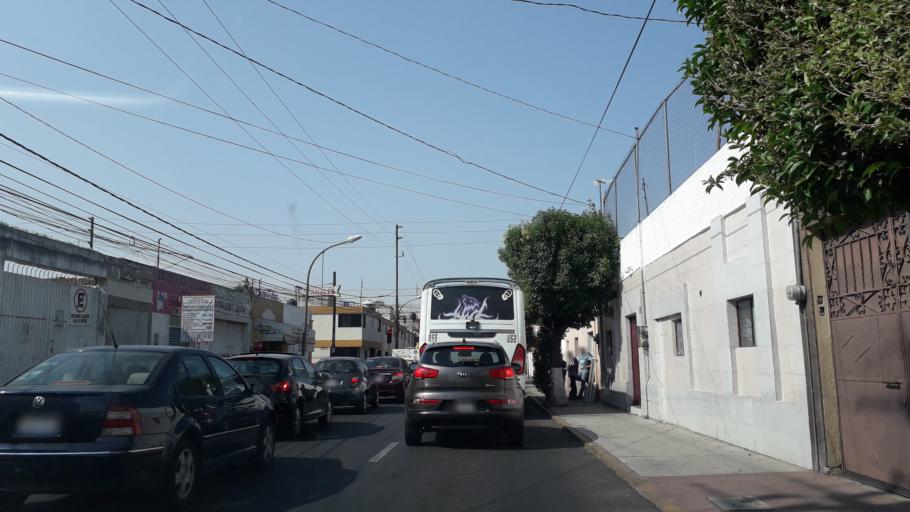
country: MX
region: Puebla
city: Puebla
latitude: 19.0432
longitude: -98.2165
